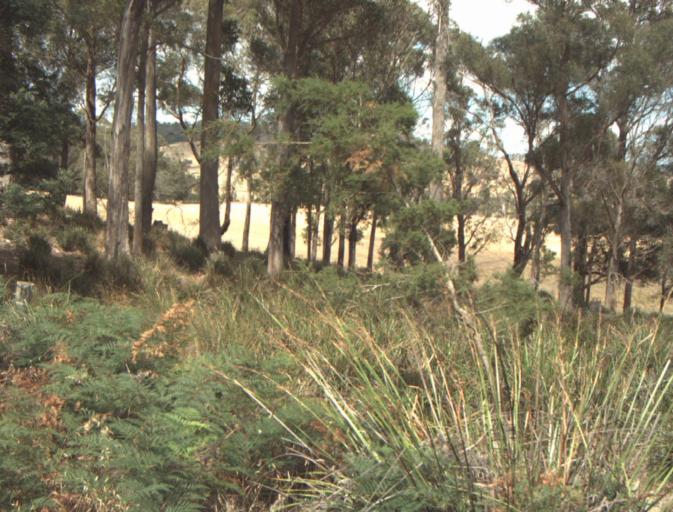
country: AU
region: Tasmania
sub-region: Launceston
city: Mayfield
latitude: -41.2096
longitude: 147.1580
